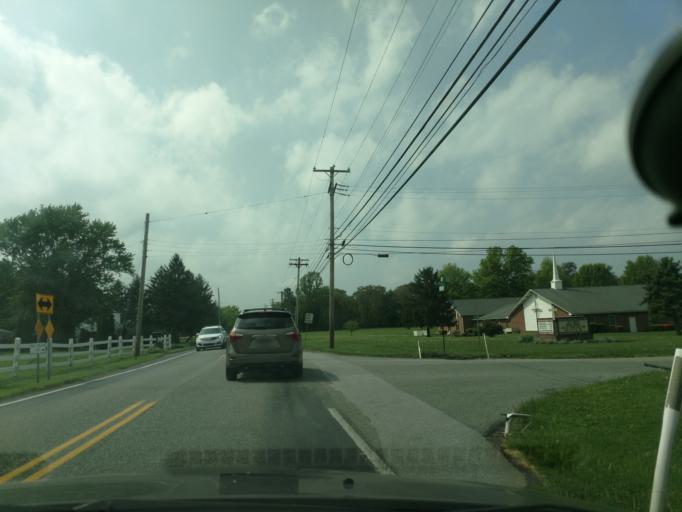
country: US
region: Pennsylvania
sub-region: Chester County
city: Spring City
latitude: 40.1664
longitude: -75.6004
